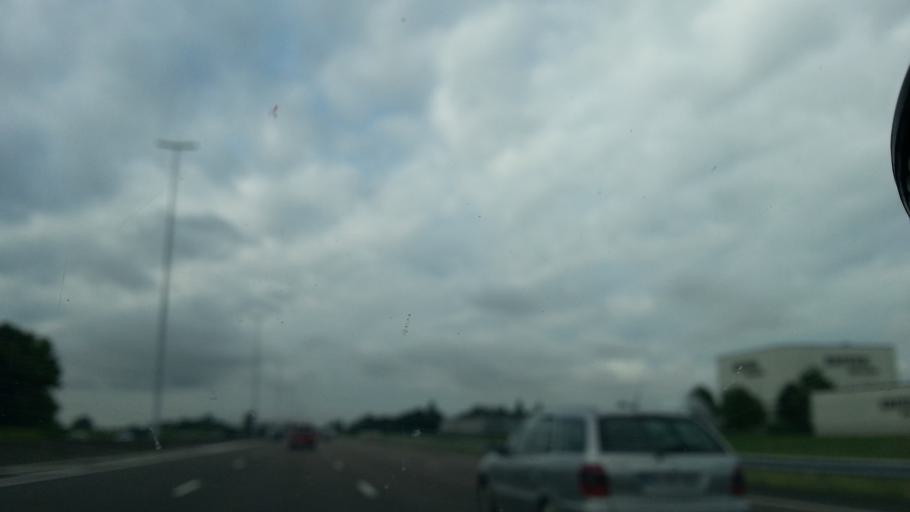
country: FR
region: Bourgogne
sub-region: Departement de la Cote-d'Or
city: Beaune
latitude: 47.0106
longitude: 4.8650
